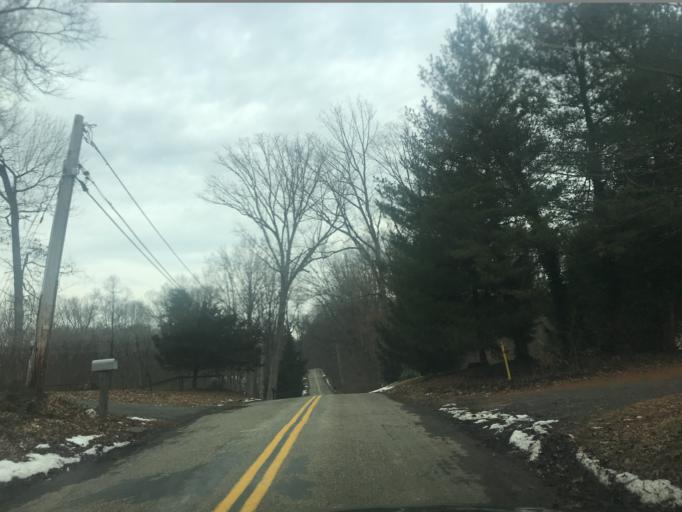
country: US
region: Maryland
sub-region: Harford County
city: Jarrettsville
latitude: 39.6512
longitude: -76.4067
